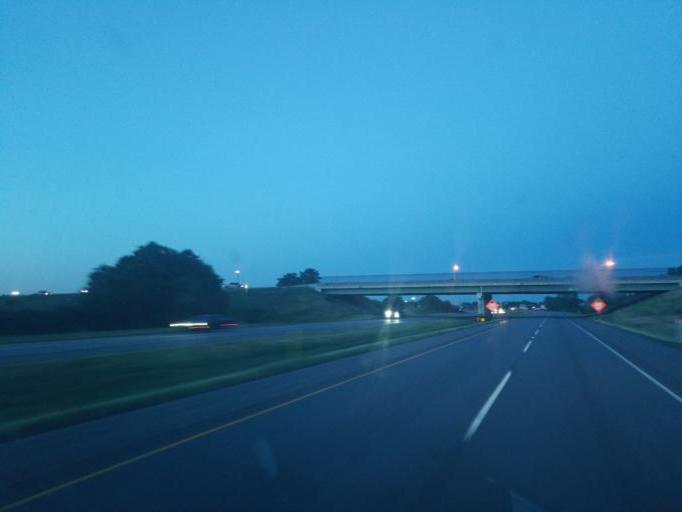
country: US
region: Indiana
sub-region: Saint Joseph County
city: Georgetown
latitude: 41.7162
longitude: -86.1793
